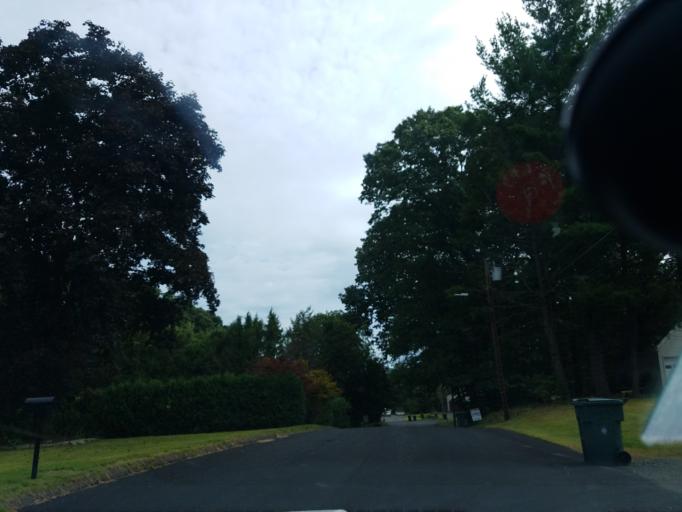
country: US
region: Connecticut
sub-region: Hartford County
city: Glastonbury Center
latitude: 41.6552
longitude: -72.6298
